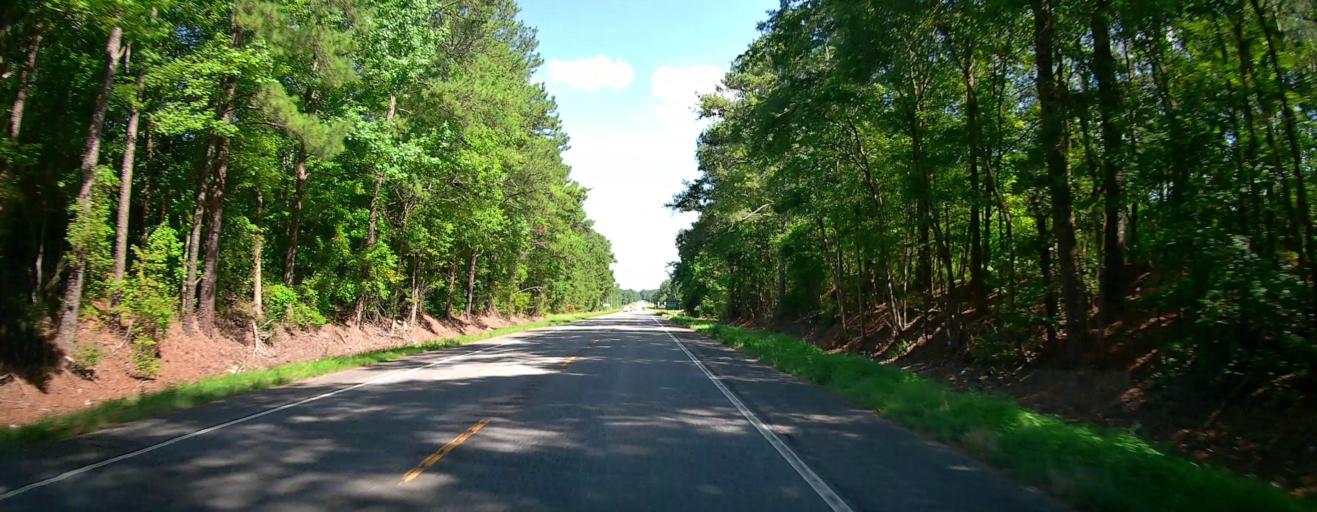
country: US
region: Alabama
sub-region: Pickens County
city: Gordo
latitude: 33.3061
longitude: -87.8862
